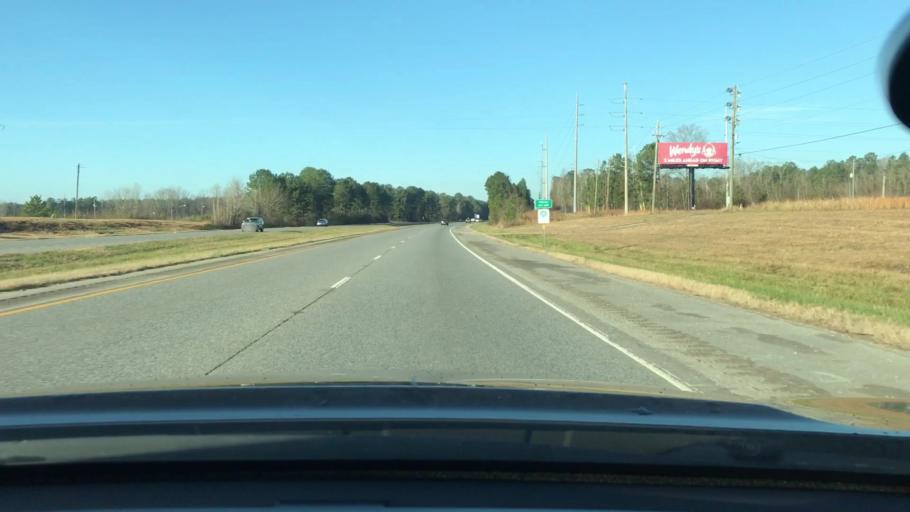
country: US
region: Alabama
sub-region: Shelby County
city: Westover
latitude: 33.3486
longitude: -86.5662
